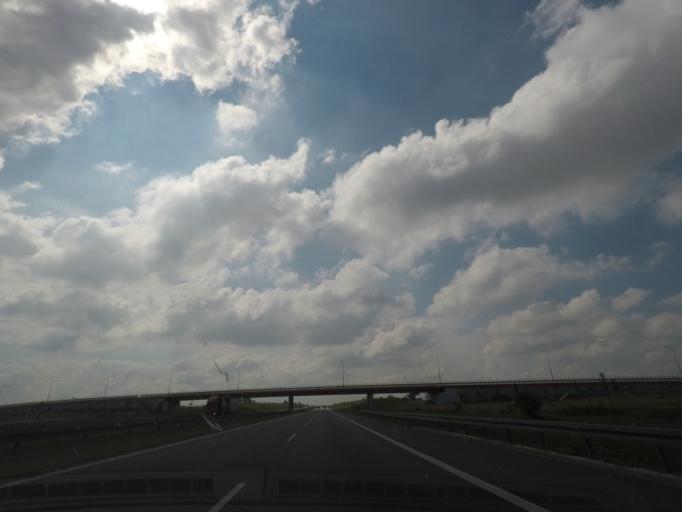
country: PL
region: Lodz Voivodeship
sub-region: Powiat kutnowski
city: Krzyzanow
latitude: 52.1702
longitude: 19.4848
